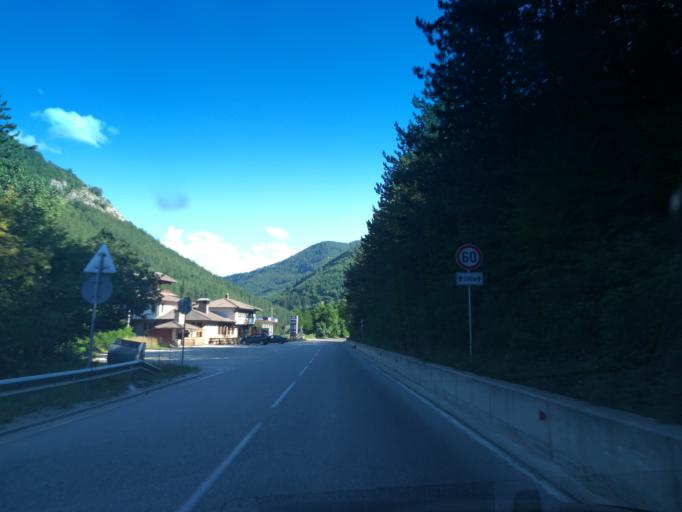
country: BG
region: Smolyan
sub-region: Obshtina Chepelare
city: Chepelare
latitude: 41.8422
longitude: 24.6789
